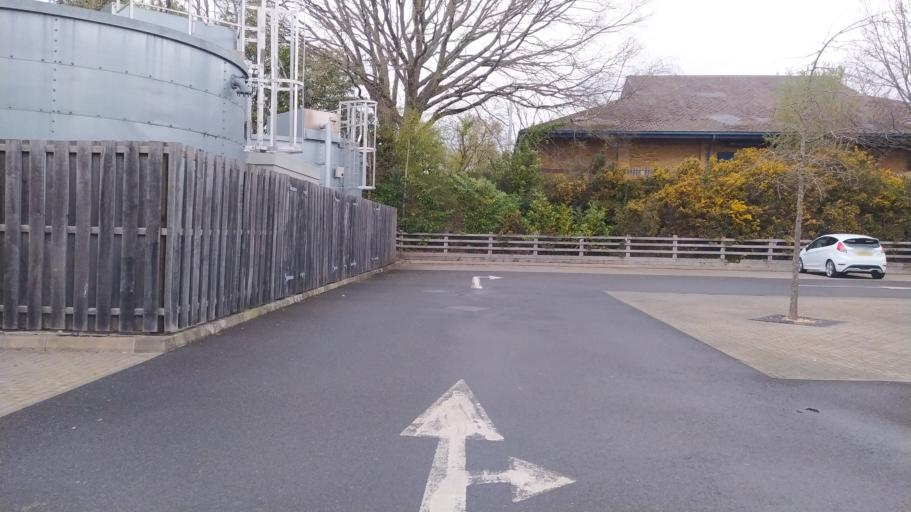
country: GB
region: England
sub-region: Hampshire
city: Hedge End
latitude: 50.9169
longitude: -1.3125
